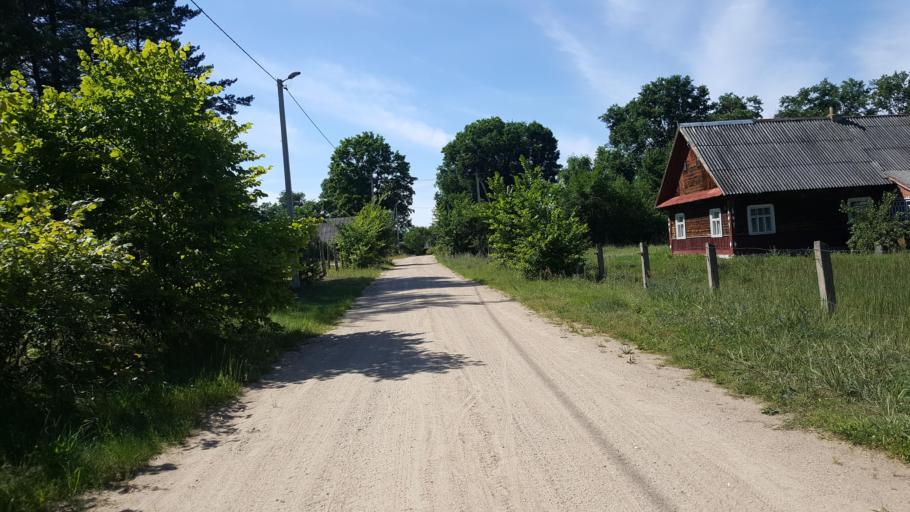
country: BY
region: Brest
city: Zhabinka
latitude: 52.4614
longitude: 24.1127
